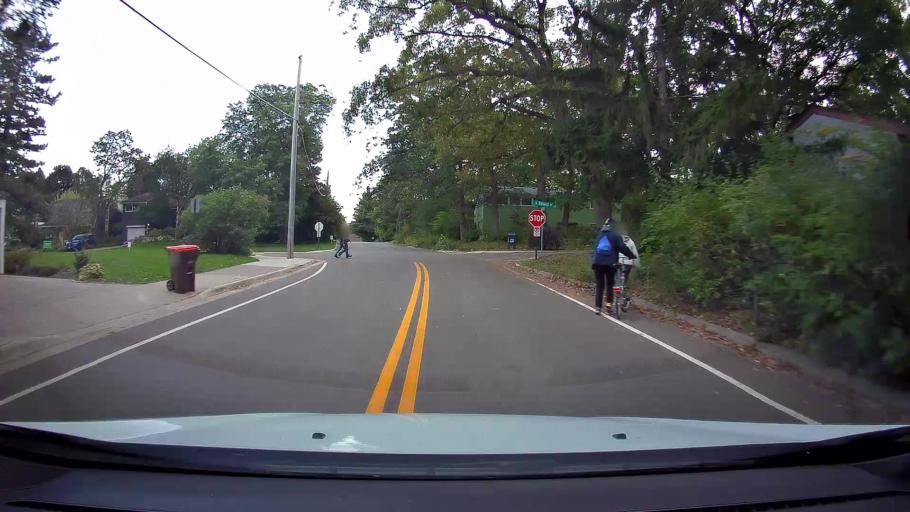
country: US
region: Minnesota
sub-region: Ramsey County
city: Lauderdale
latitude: 44.9904
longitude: -93.1885
